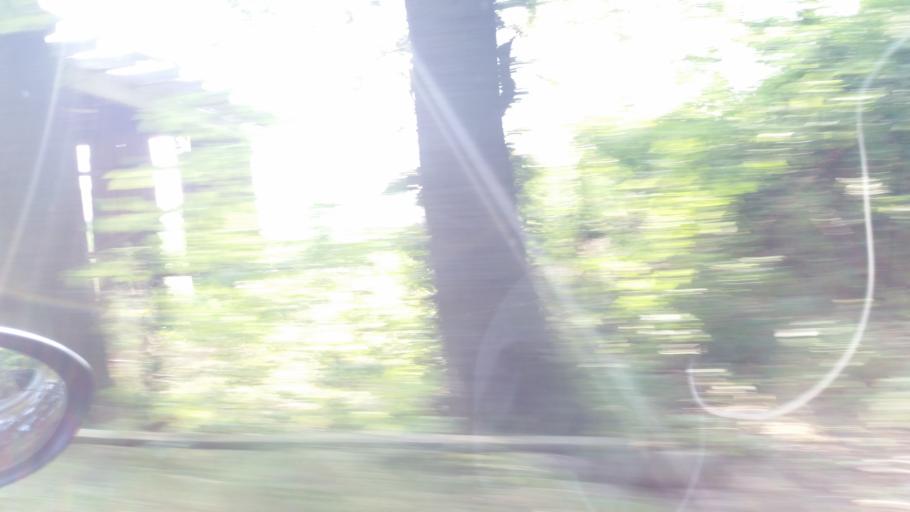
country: DE
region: Baden-Wuerttemberg
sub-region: Karlsruhe Region
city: Osterburken
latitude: 49.4263
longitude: 9.4535
